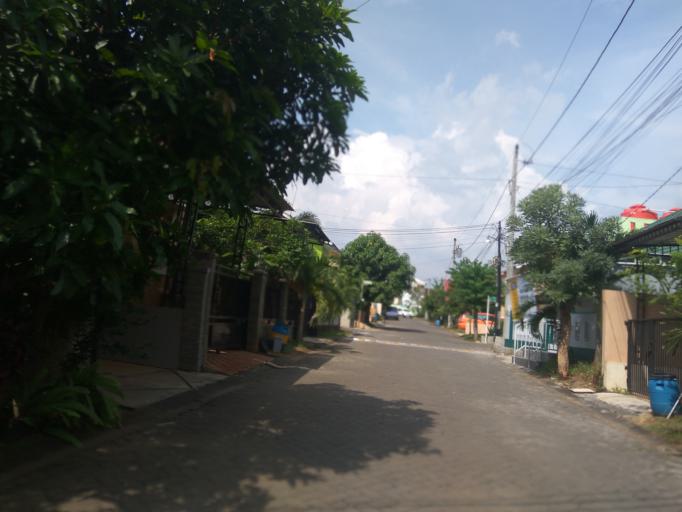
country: ID
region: Central Java
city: Ungaran
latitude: -7.0730
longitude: 110.4444
